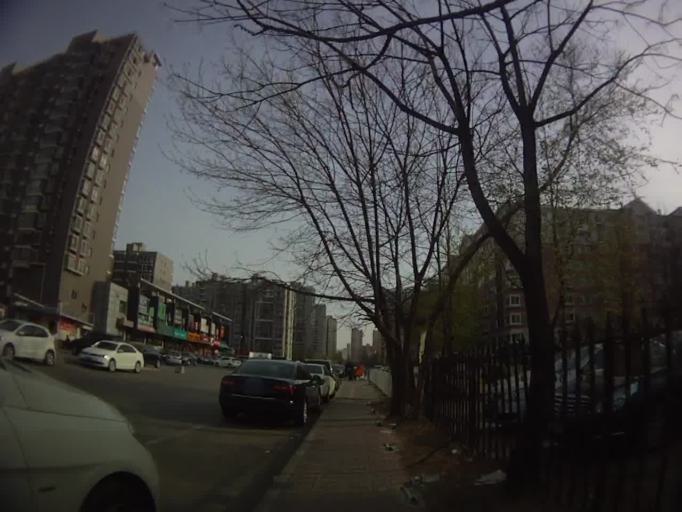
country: CN
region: Beijing
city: Longtan
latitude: 39.8976
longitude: 116.4441
